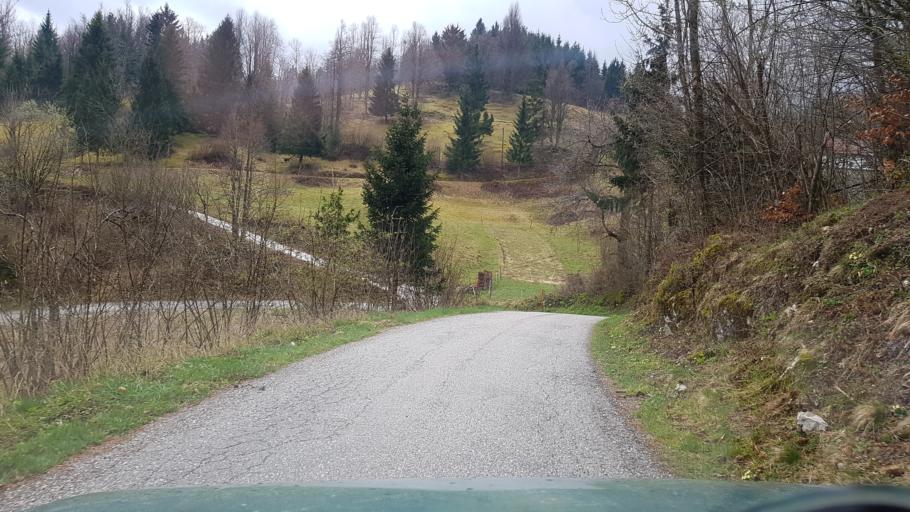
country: SI
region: Cerkno
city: Cerkno
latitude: 46.1425
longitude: 13.8832
